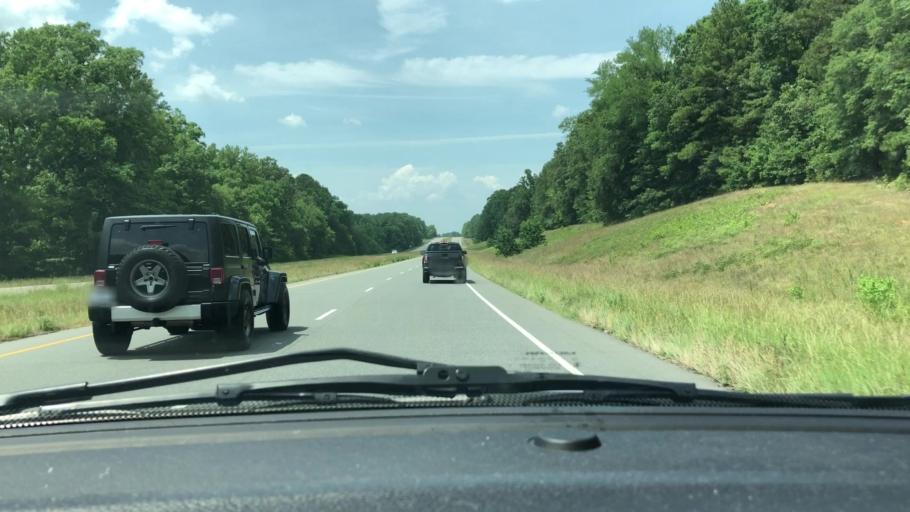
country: US
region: North Carolina
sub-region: Chatham County
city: Farmville
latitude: 35.5295
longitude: -79.2324
